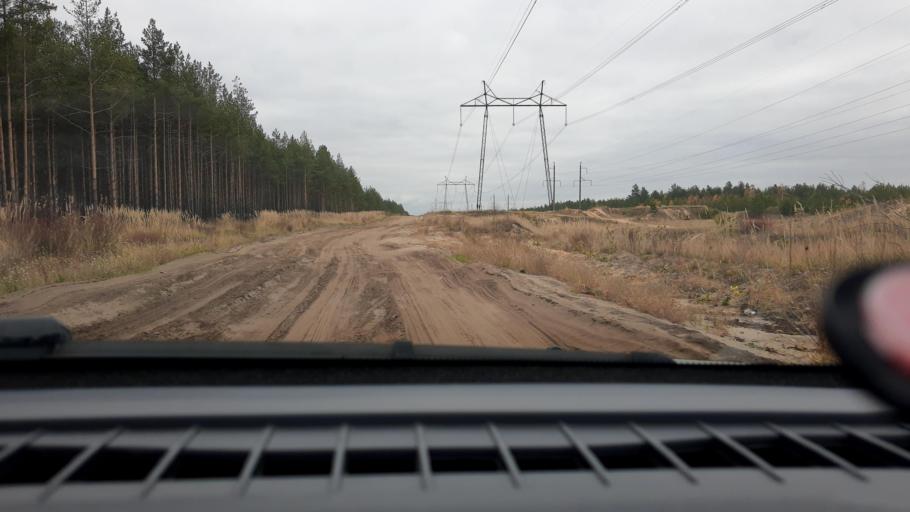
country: RU
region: Nizjnij Novgorod
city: Lukino
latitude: 56.3882
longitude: 43.6430
